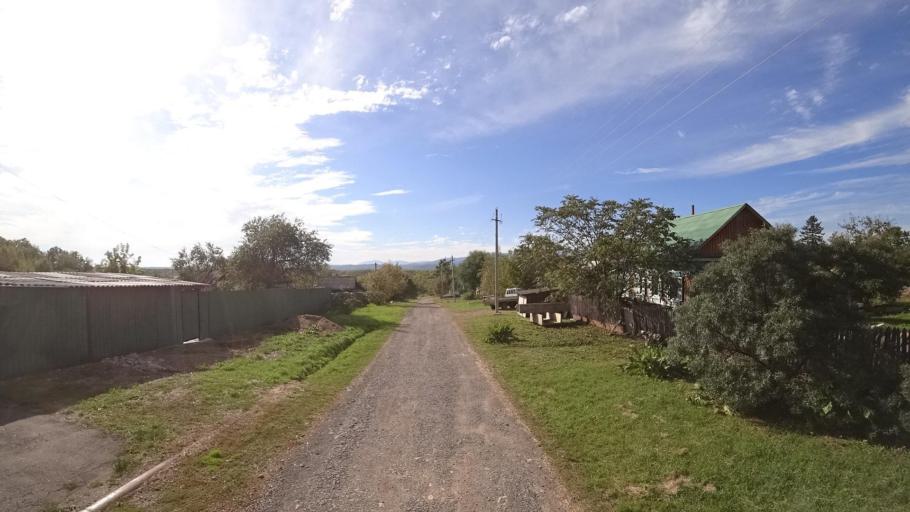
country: RU
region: Primorskiy
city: Dostoyevka
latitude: 44.3056
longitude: 133.4498
